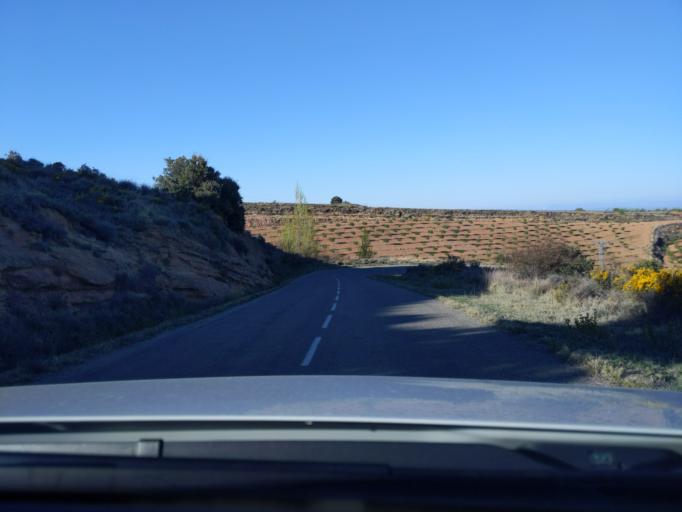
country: ES
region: La Rioja
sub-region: Provincia de La Rioja
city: Bergasillas Bajera
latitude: 42.2461
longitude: -2.1457
